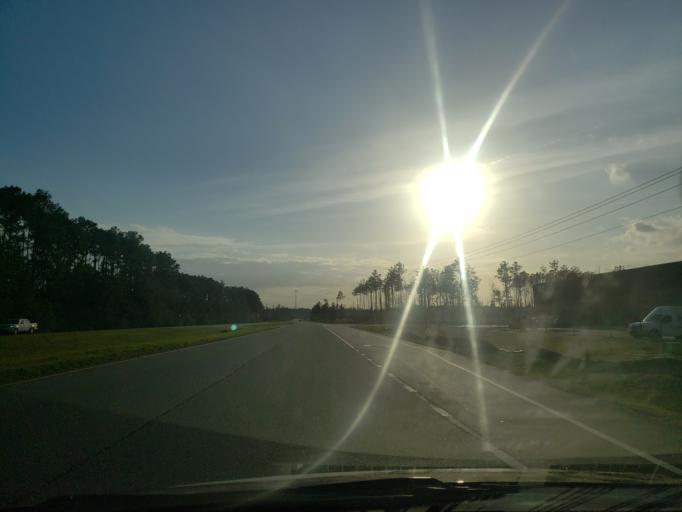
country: US
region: Georgia
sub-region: Chatham County
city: Bloomingdale
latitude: 32.1569
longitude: -81.2737
